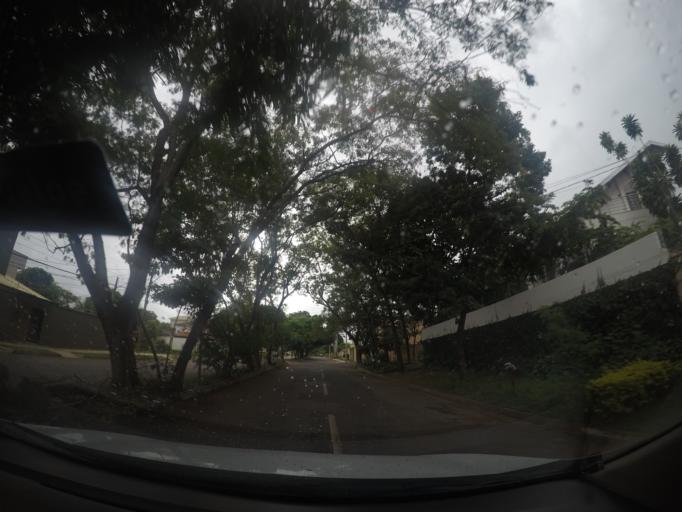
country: BR
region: Goias
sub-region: Goiania
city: Goiania
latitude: -16.6400
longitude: -49.2264
